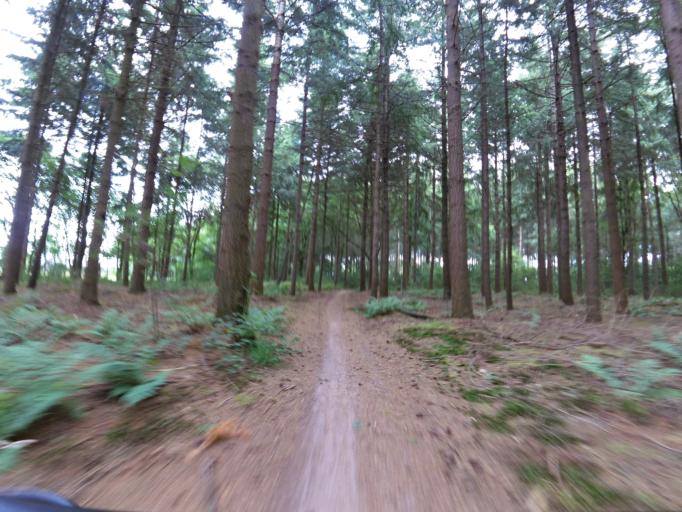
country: NL
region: North Brabant
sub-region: Gemeente Son en Breugel
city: Breugel
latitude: 51.5567
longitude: 5.5154
